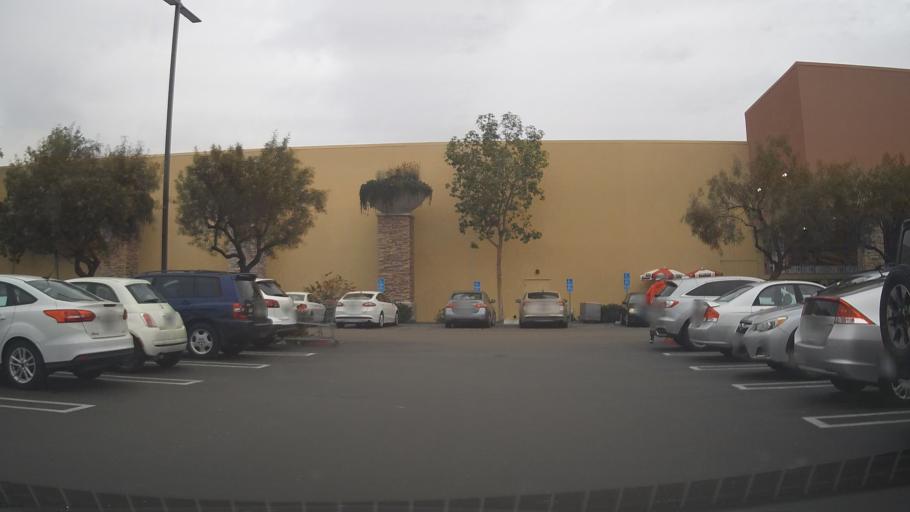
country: US
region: California
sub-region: San Diego County
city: San Diego
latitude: 32.7819
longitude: -117.1295
